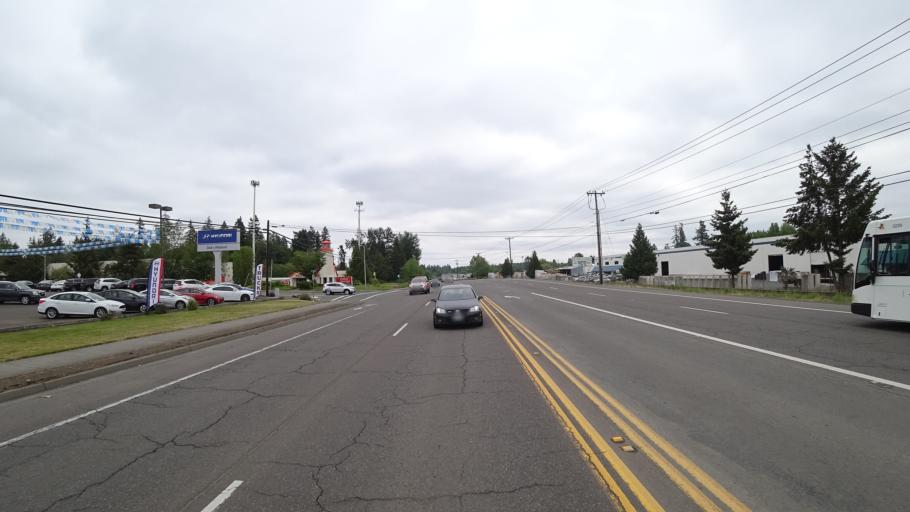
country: US
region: Oregon
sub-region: Washington County
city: Hillsboro
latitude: 45.5034
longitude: -122.9530
